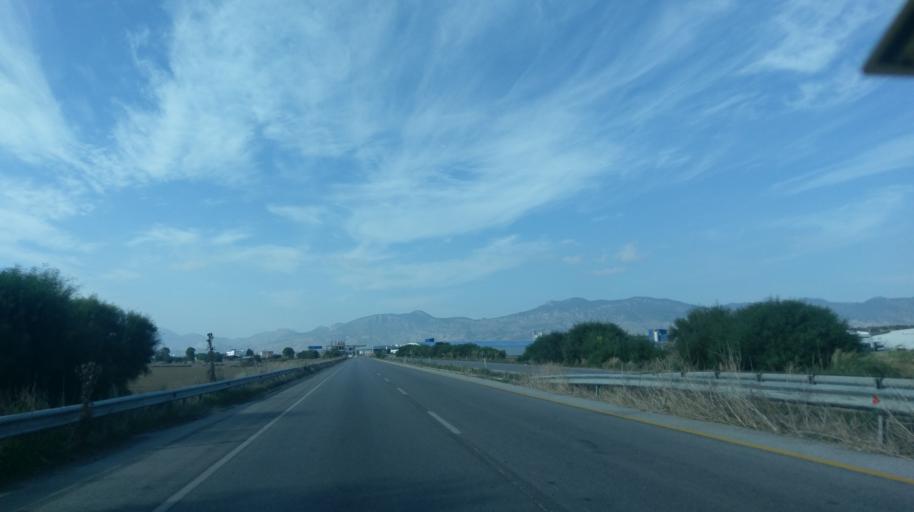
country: CY
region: Ammochostos
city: Lefkonoiko
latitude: 35.2035
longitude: 33.5991
